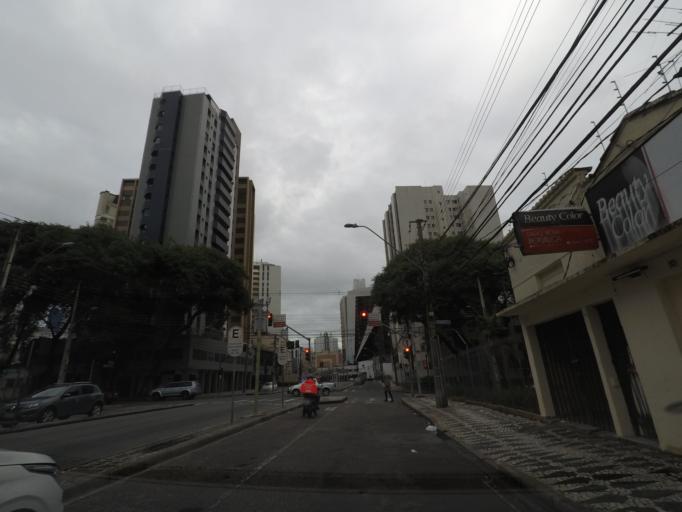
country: BR
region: Parana
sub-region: Curitiba
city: Curitiba
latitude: -25.4542
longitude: -49.2879
